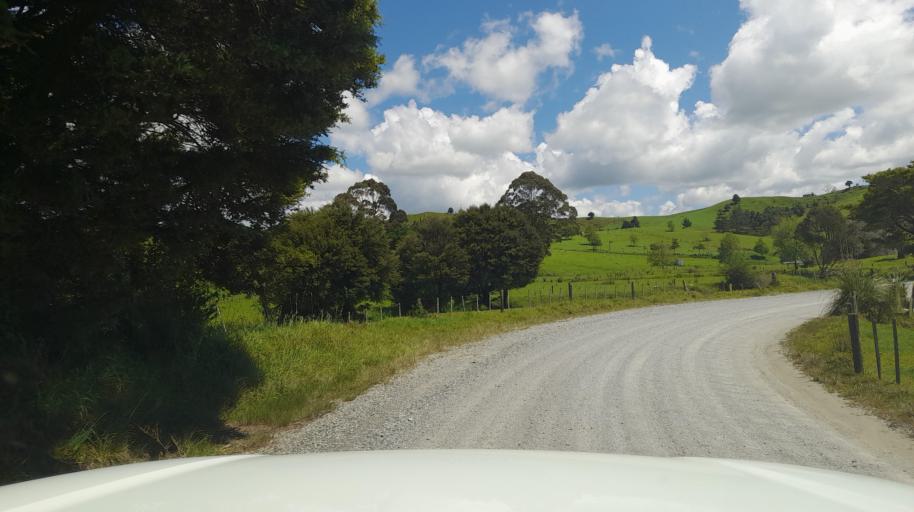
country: NZ
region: Northland
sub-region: Far North District
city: Kaitaia
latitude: -35.1212
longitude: 173.4022
